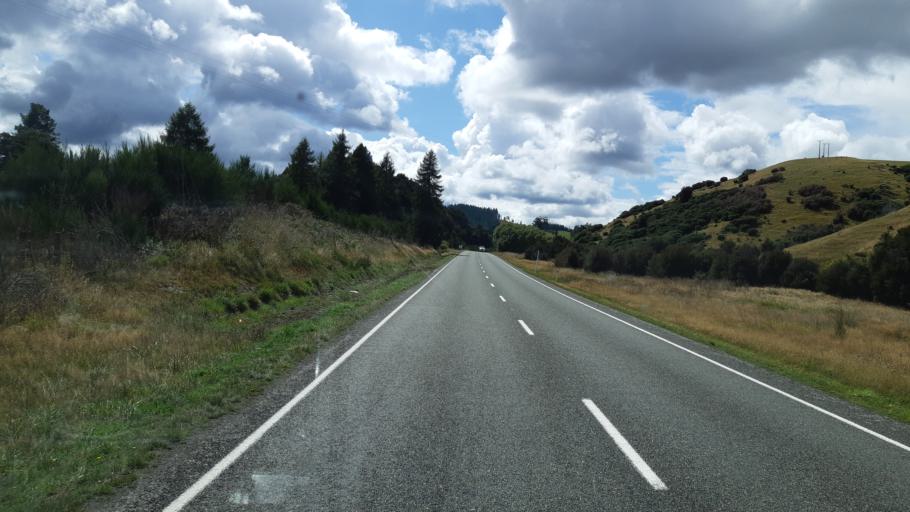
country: NZ
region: Tasman
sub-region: Tasman District
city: Wakefield
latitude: -41.6479
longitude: 172.6523
